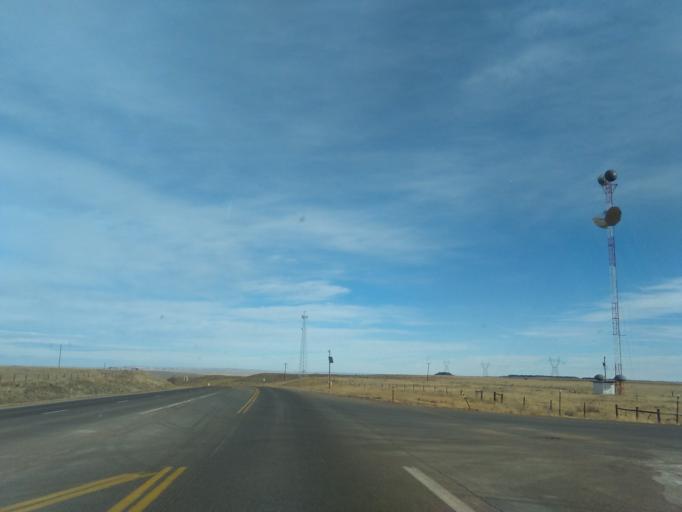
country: US
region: Wyoming
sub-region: Laramie County
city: Pine Bluffs
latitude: 41.4416
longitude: -104.3462
